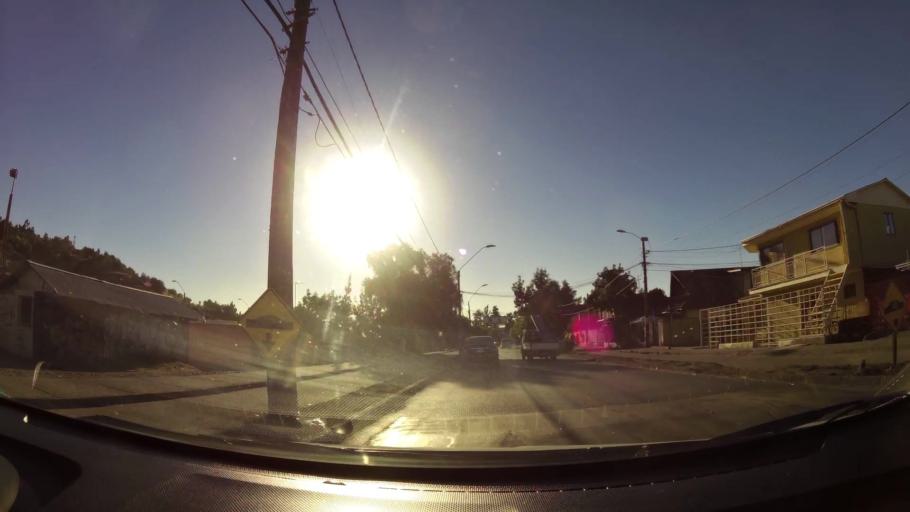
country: CL
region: Maule
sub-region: Provincia de Curico
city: Curico
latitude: -34.9747
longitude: -71.2247
